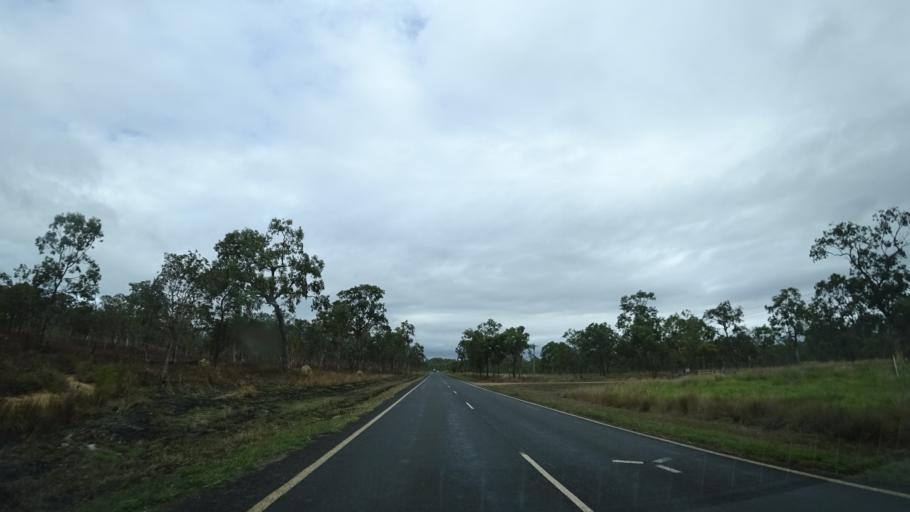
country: AU
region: Queensland
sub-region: Tablelands
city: Mareeba
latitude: -16.7669
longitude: 145.3410
